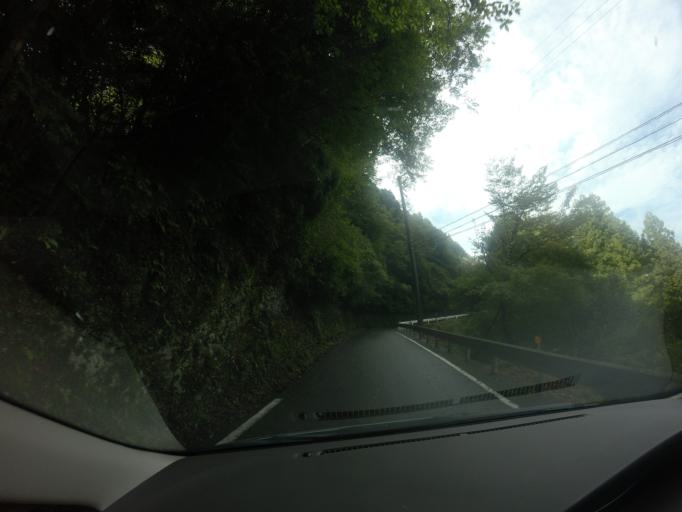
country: JP
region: Wakayama
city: Shingu
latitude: 33.9652
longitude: 135.8492
